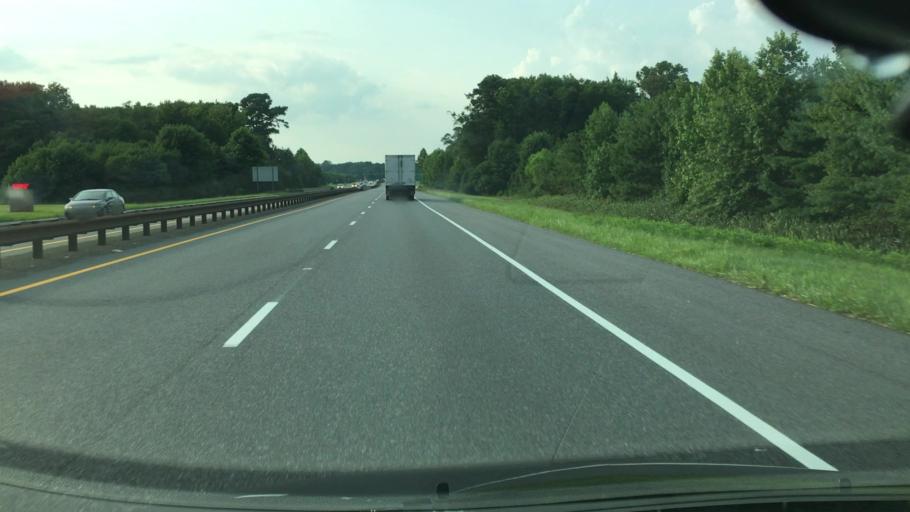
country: US
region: Maryland
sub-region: Worcester County
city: Ocean Pines
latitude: 38.3993
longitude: -75.2079
